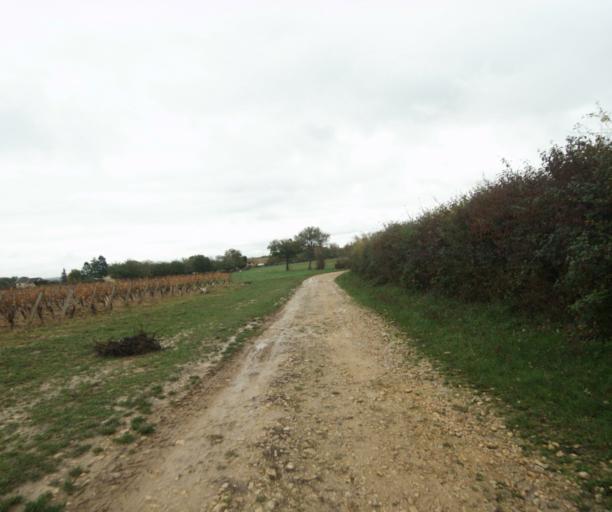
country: FR
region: Bourgogne
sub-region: Departement de Saone-et-Loire
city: Tournus
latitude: 46.4859
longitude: 4.8632
